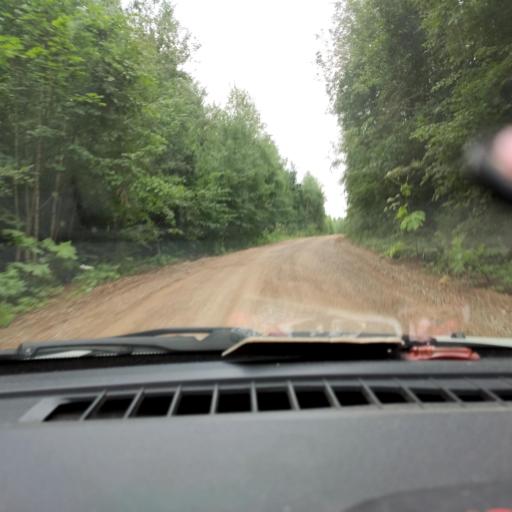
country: RU
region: Perm
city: Kultayevo
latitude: 57.8069
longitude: 56.0042
